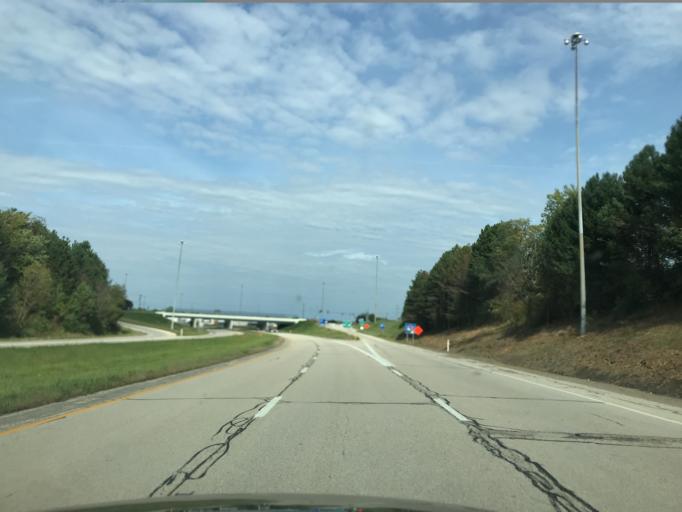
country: US
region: Ohio
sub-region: Ashtabula County
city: Edgewood
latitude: 41.8732
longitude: -80.7611
